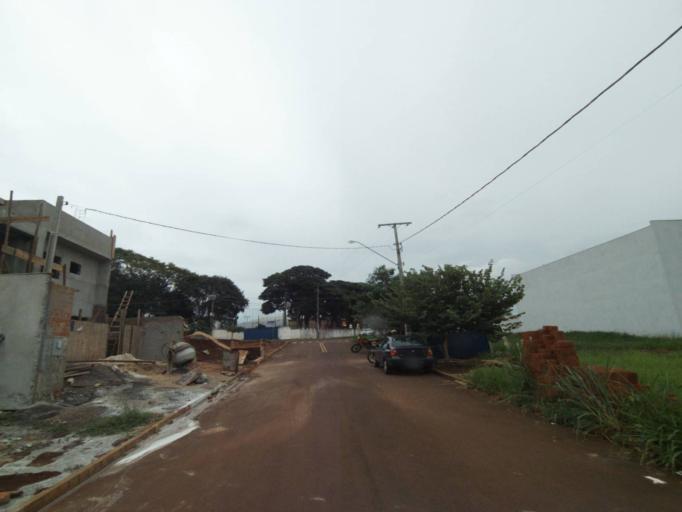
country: BR
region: Parana
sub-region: Campo Mourao
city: Campo Mourao
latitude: -24.0363
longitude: -52.3619
